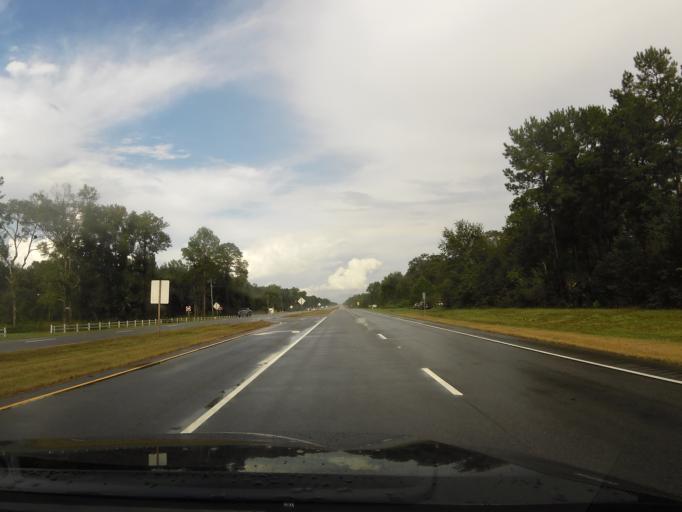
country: US
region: Georgia
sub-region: Long County
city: Ludowici
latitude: 31.7308
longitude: -81.7126
